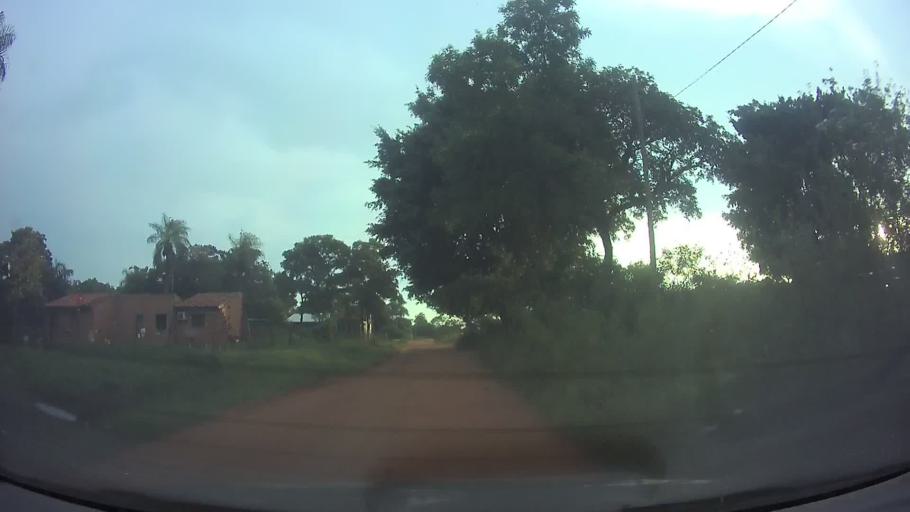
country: PY
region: Central
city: Limpio
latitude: -25.2441
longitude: -57.4495
